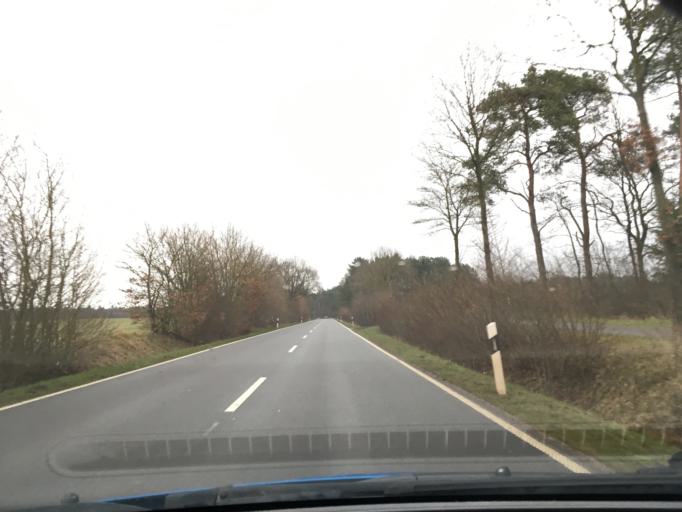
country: DE
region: Schleswig-Holstein
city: Roseburg
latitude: 53.5351
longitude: 10.6305
